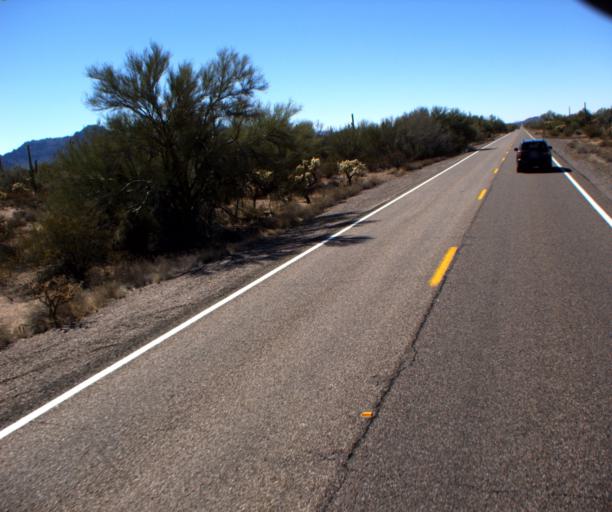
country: US
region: Arizona
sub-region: Pima County
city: Ajo
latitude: 32.1684
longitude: -112.7632
